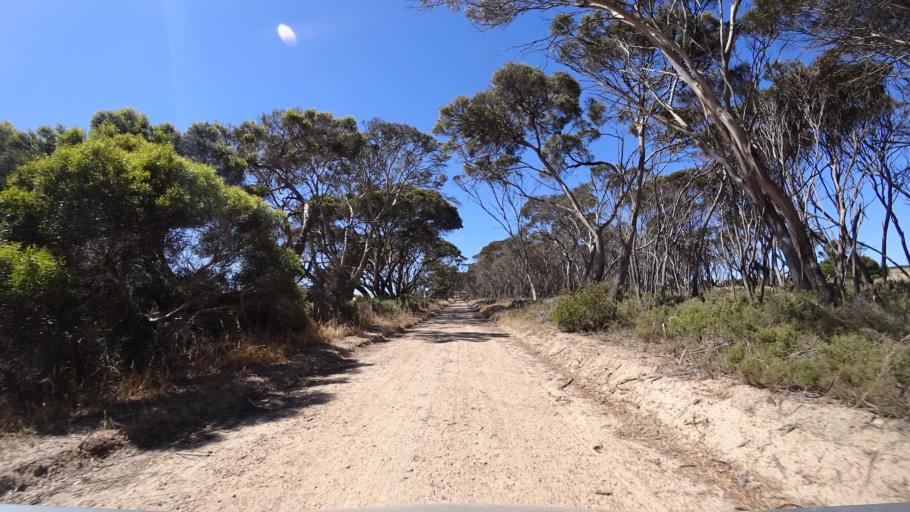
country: AU
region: South Australia
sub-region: Kangaroo Island
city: Kingscote
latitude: -35.7387
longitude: 137.7199
